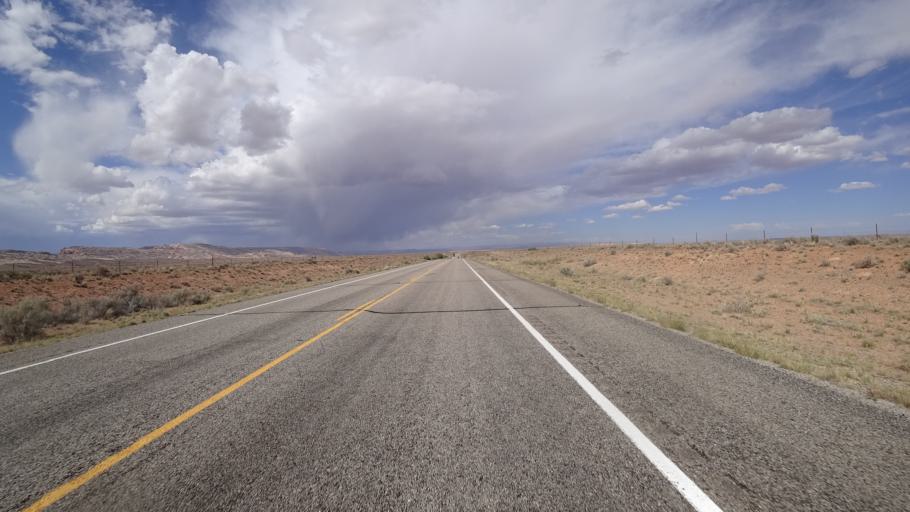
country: US
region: Utah
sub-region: Emery County
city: Castle Dale
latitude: 38.6776
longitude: -110.5350
